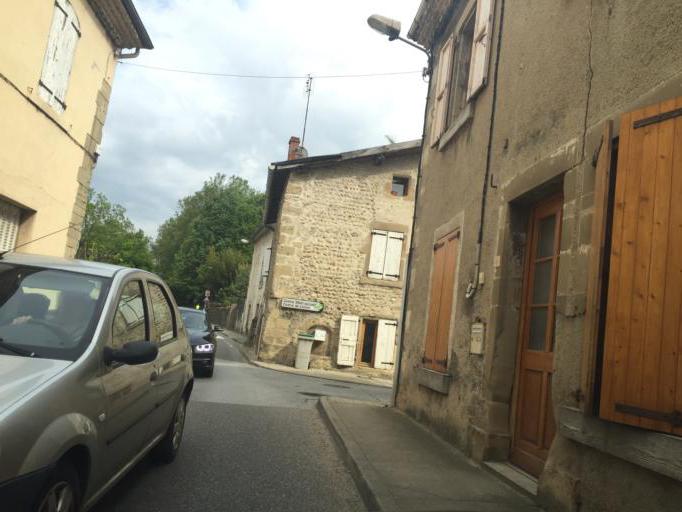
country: FR
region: Rhone-Alpes
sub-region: Departement de la Drome
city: Alixan
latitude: 44.9748
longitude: 5.0280
